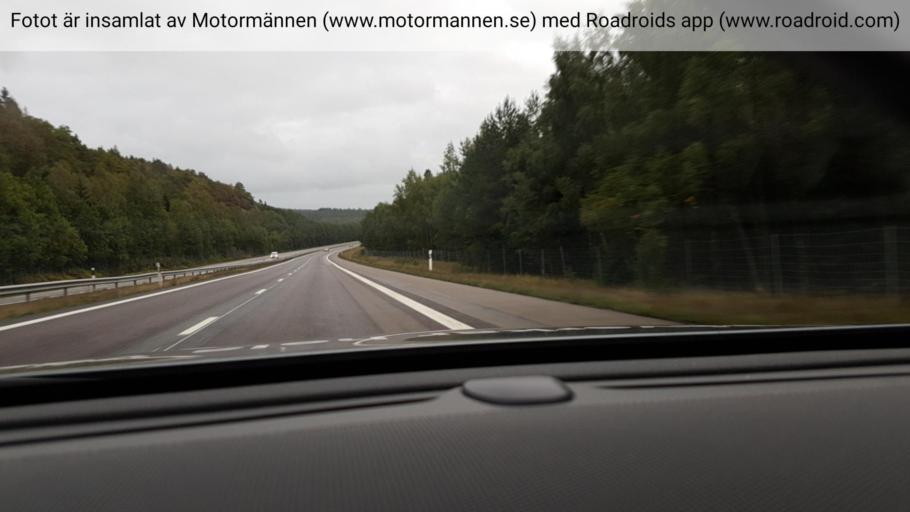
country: SE
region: Vaestra Goetaland
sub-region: Stenungsunds Kommun
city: Stenungsund
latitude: 58.0757
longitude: 11.8858
